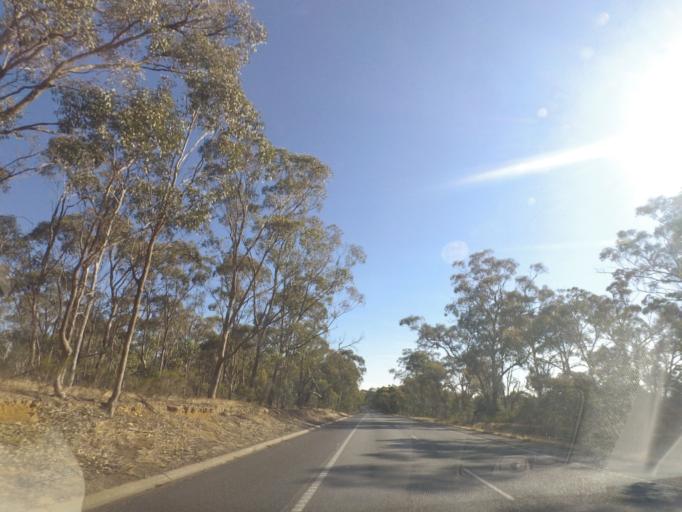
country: AU
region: Victoria
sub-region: Murrindindi
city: Kinglake West
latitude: -37.1753
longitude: 145.0728
